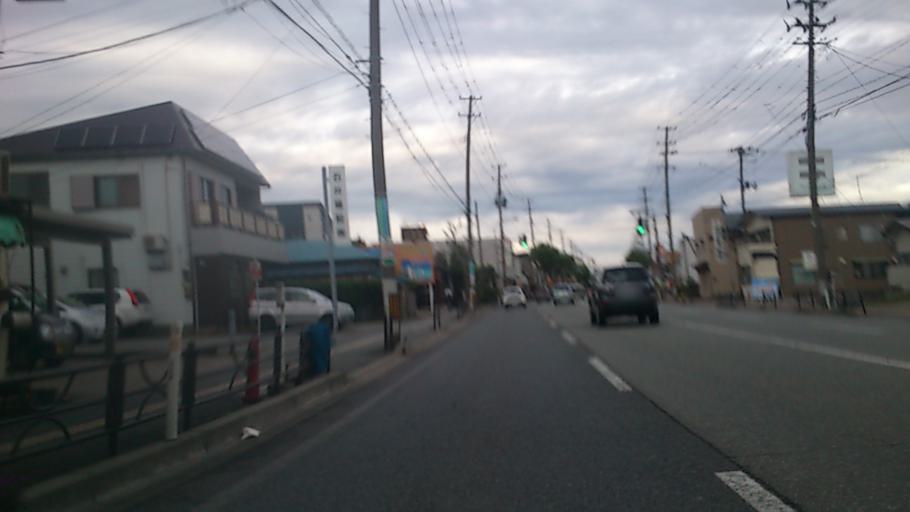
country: JP
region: Akita
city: Akita Shi
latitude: 39.7485
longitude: 140.0753
